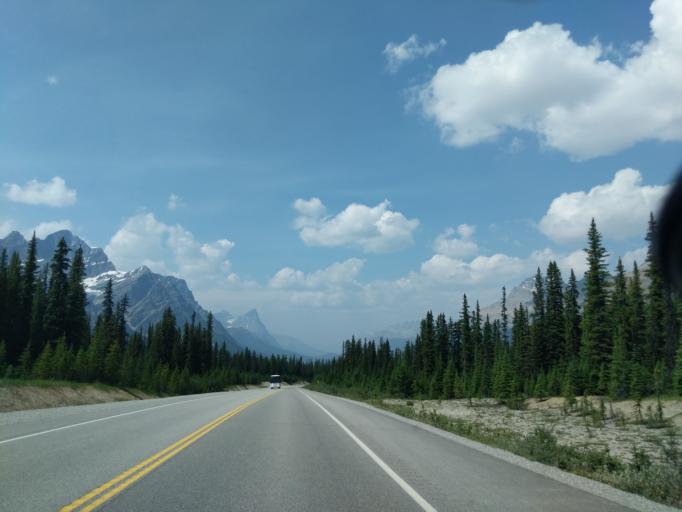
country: CA
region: Alberta
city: Lake Louise
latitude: 51.7217
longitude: -116.4965
